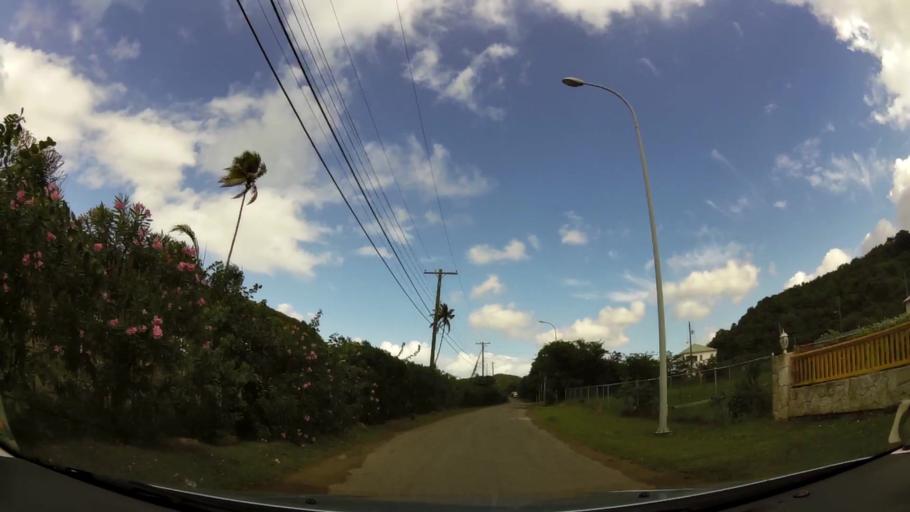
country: AG
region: Saint John
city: Saint John's
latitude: 17.1187
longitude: -61.8883
